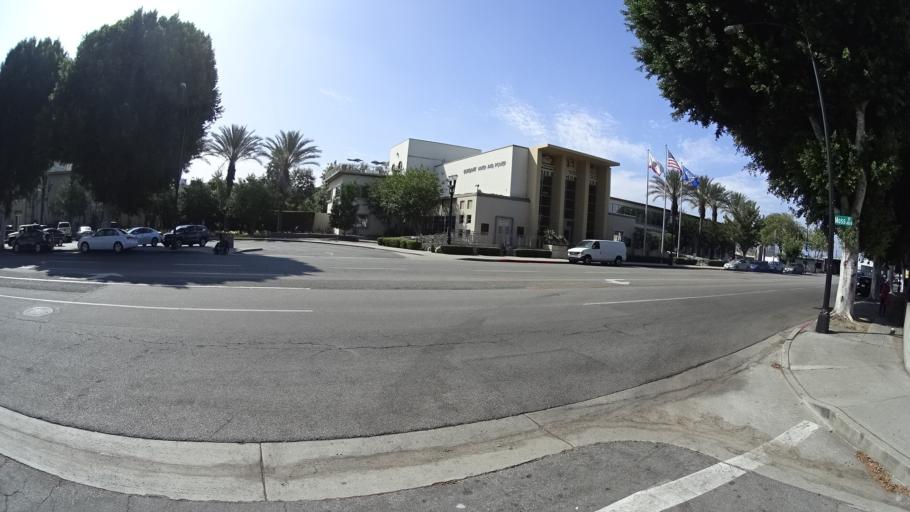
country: US
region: California
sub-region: Los Angeles County
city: Burbank
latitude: 34.1784
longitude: -118.3169
